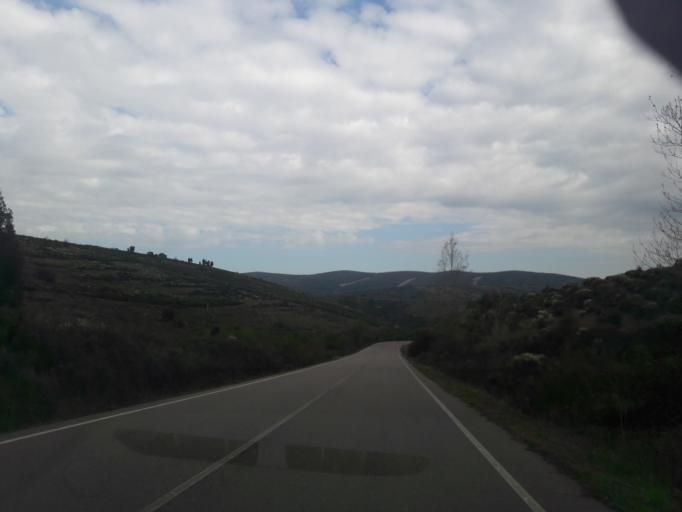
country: ES
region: Castille and Leon
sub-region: Provincia de Salamanca
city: Serradilla del Llano
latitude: 40.5086
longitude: -6.3628
